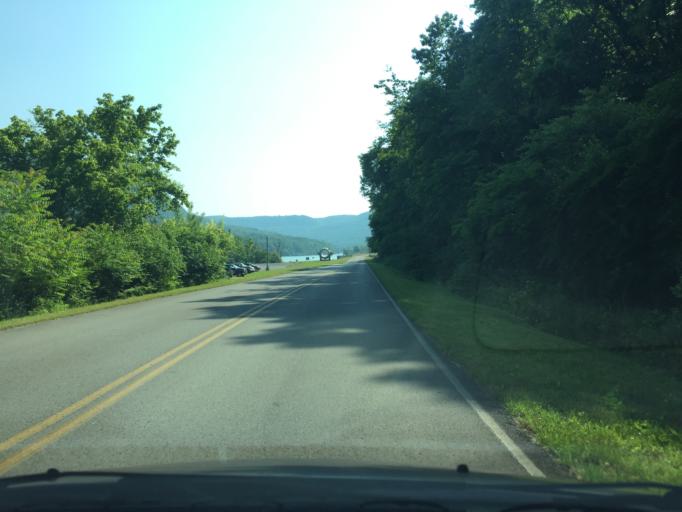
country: US
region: Tennessee
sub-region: Hamilton County
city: Lookout Mountain
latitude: 35.0592
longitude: -85.4167
